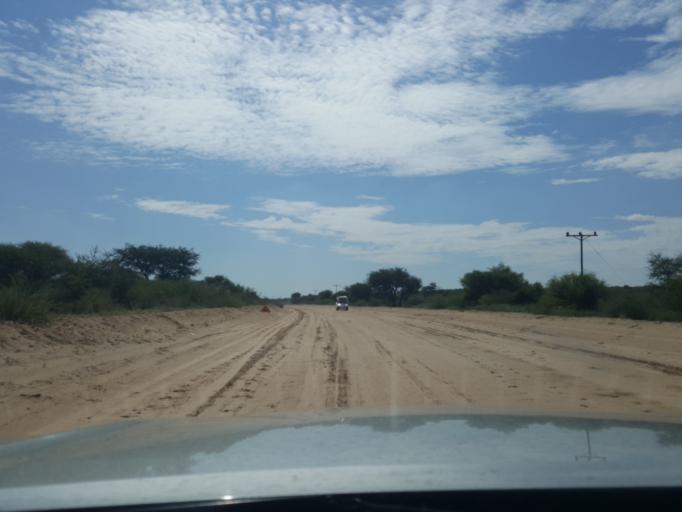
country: BW
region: Kweneng
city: Letlhakeng
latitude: -24.0482
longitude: 25.0211
